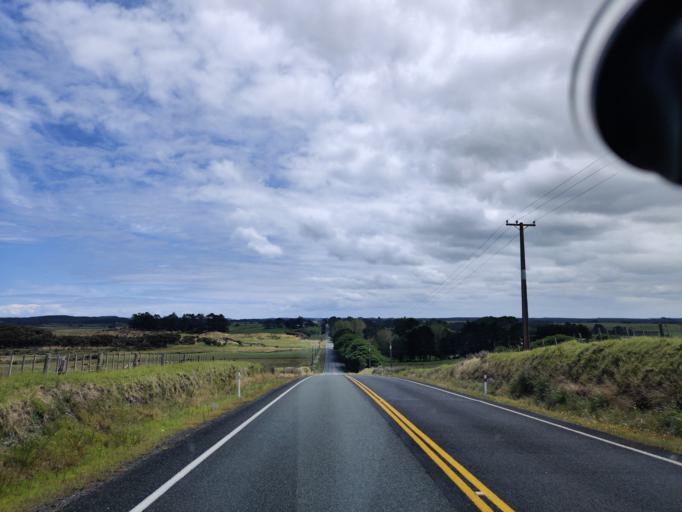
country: NZ
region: Northland
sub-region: Far North District
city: Kaitaia
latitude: -34.6844
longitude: 173.0115
